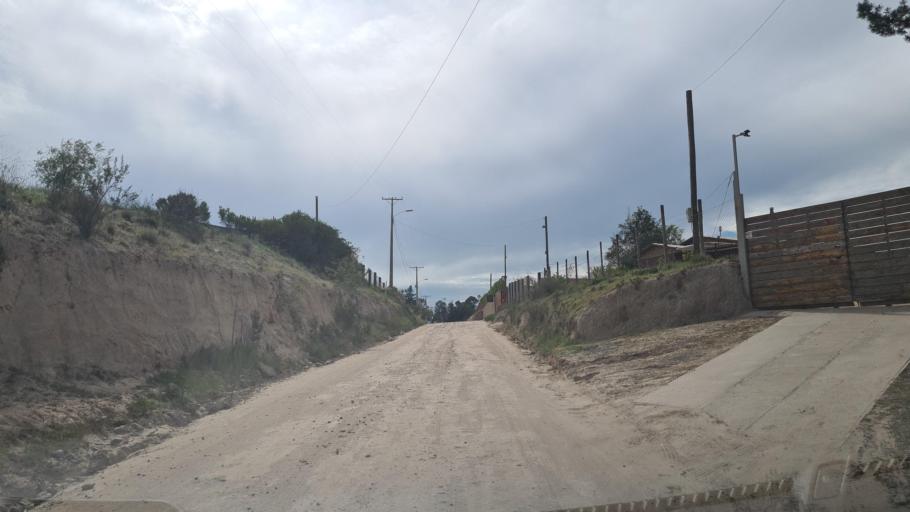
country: CL
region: O'Higgins
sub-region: Provincia de Cachapoal
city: San Vicente
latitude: -34.1503
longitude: -71.4603
